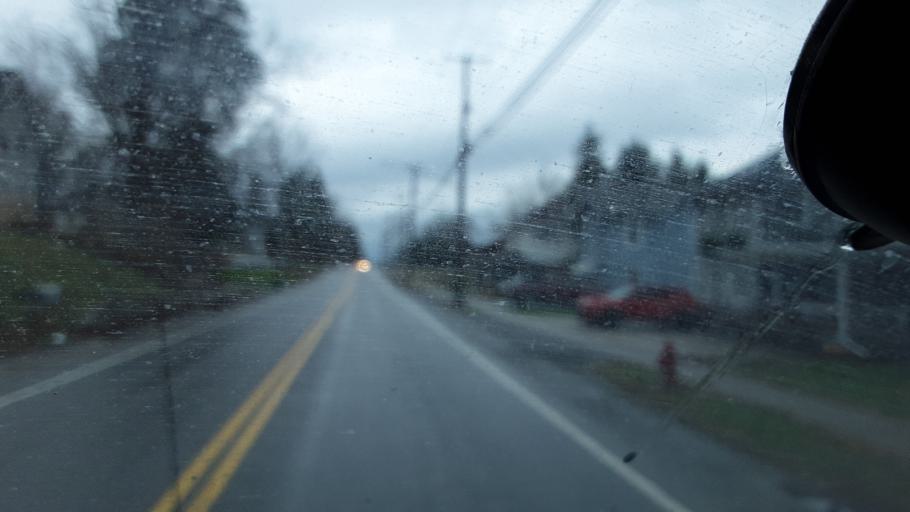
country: US
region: New York
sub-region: Erie County
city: Holland
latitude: 42.6459
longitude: -78.5482
